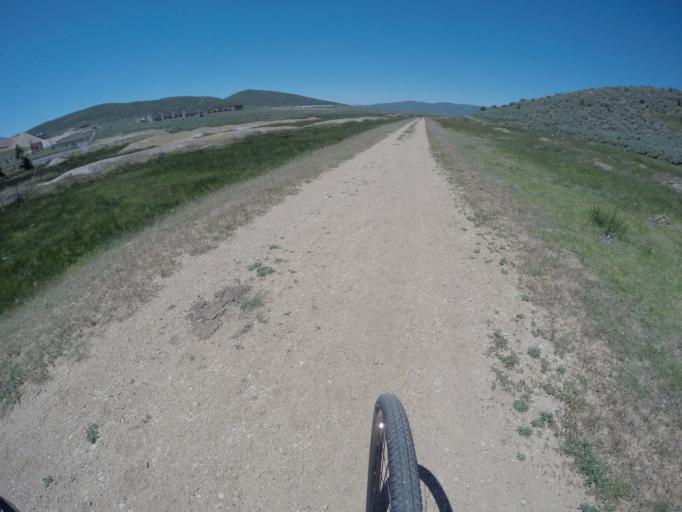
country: US
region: Utah
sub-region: Summit County
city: Park City
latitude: 40.6901
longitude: -111.4585
